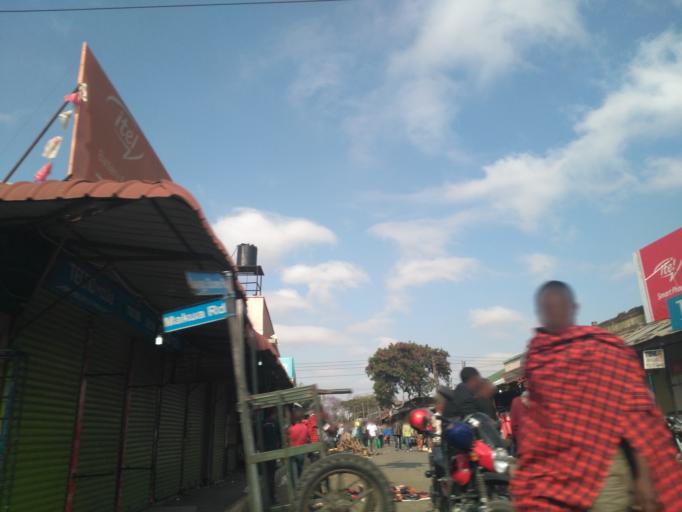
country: TZ
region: Arusha
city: Arusha
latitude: -3.3712
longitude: 36.6850
